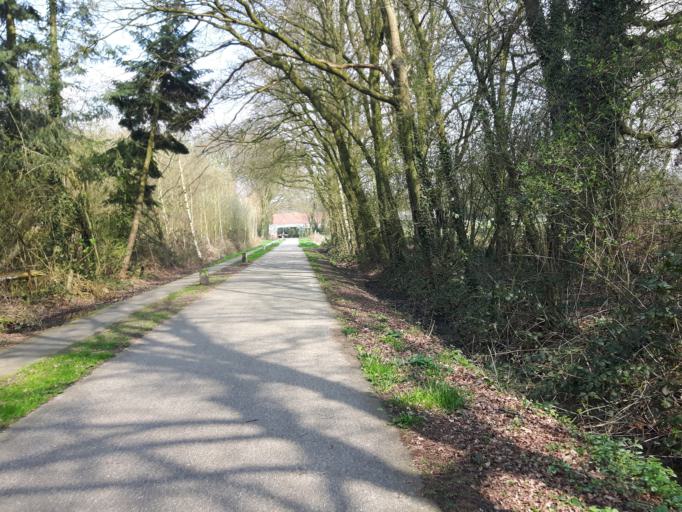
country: NL
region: Overijssel
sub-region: Gemeente Enschede
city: Enschede
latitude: 52.1885
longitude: 6.8466
